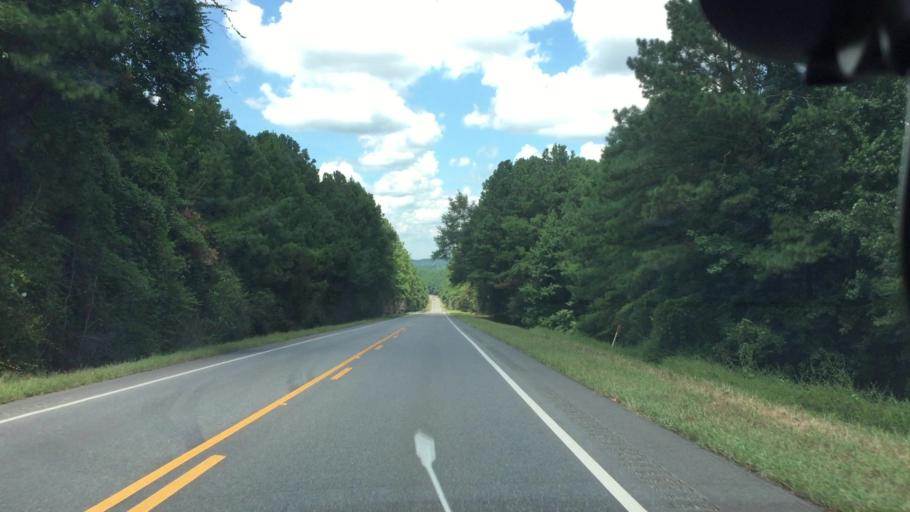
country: US
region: Alabama
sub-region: Coffee County
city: New Brockton
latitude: 31.4537
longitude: -85.8964
